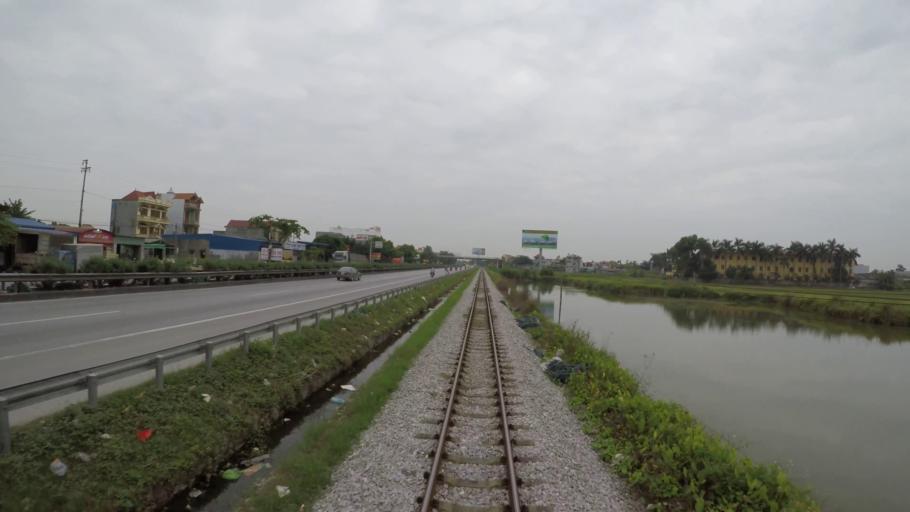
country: VN
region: Hai Duong
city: Phu Thai
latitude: 20.9233
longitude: 106.5585
